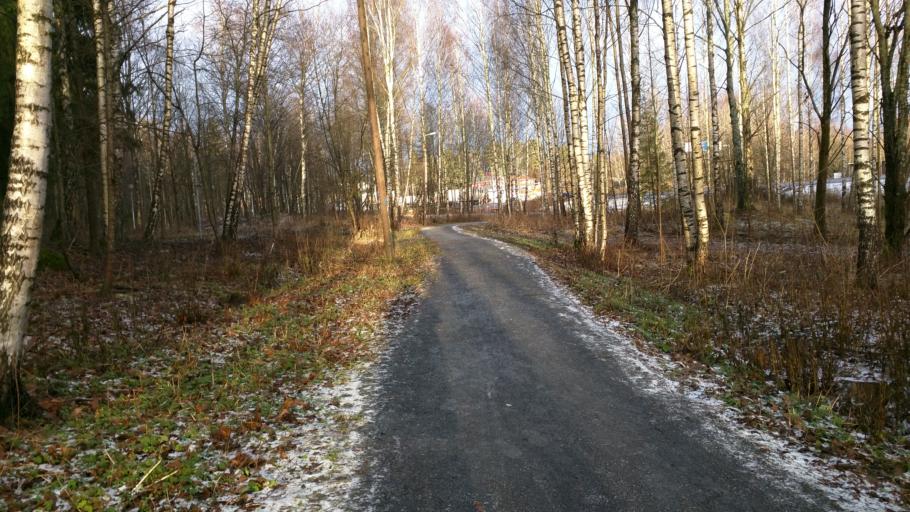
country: FI
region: Uusimaa
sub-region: Helsinki
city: Kilo
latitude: 60.2623
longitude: 24.8096
